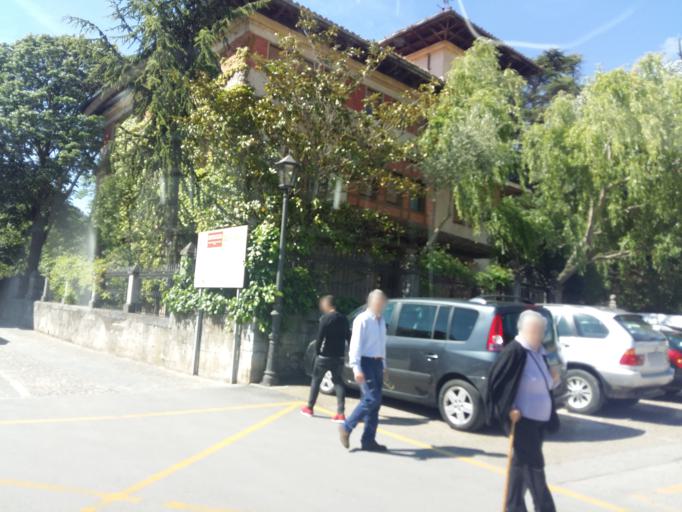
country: ES
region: Cantabria
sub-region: Provincia de Cantabria
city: Potes
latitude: 43.1542
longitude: -4.6255
